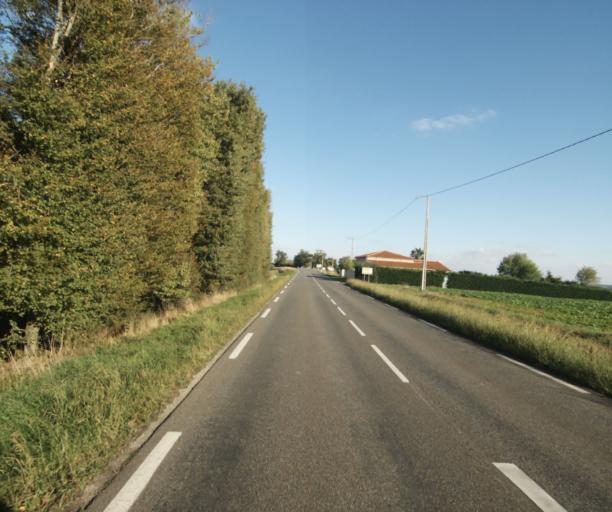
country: FR
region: Midi-Pyrenees
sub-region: Departement du Gers
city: Eauze
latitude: 43.7700
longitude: 0.1333
